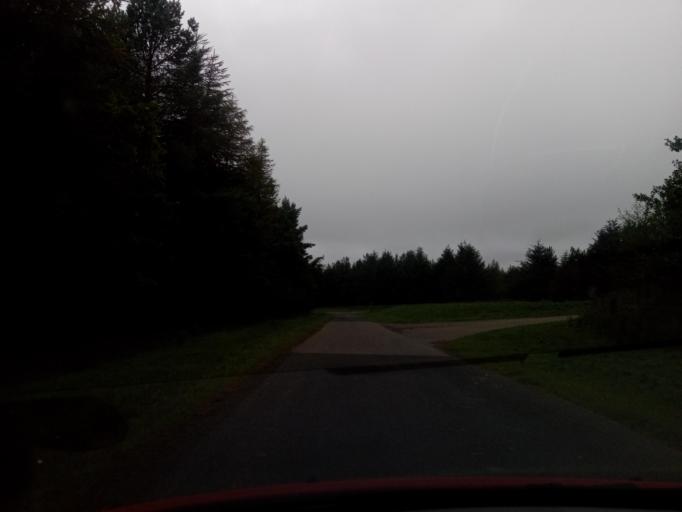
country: GB
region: England
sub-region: Northumberland
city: Otterburn
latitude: 55.2630
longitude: -2.1194
